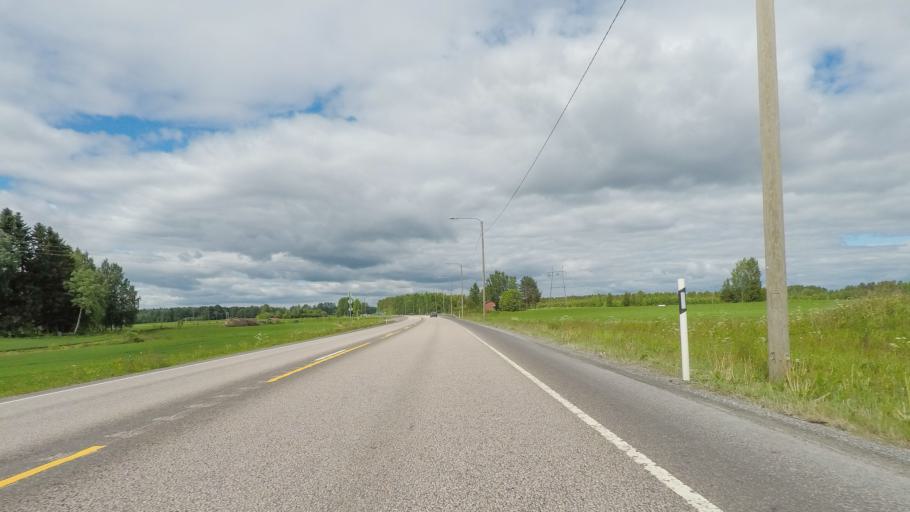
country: FI
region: Paijanne Tavastia
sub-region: Lahti
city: Hartola
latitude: 61.6042
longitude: 26.0090
